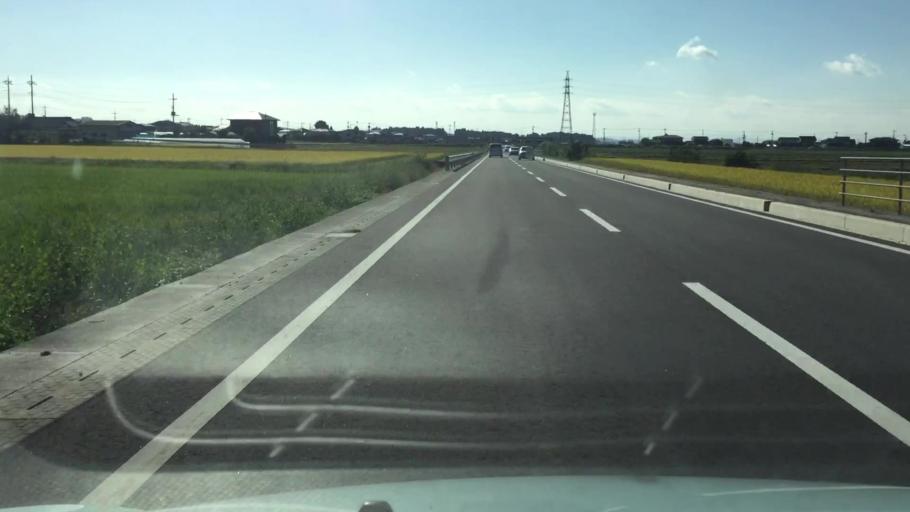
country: JP
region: Tochigi
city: Ujiie
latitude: 36.6599
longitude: 140.0197
